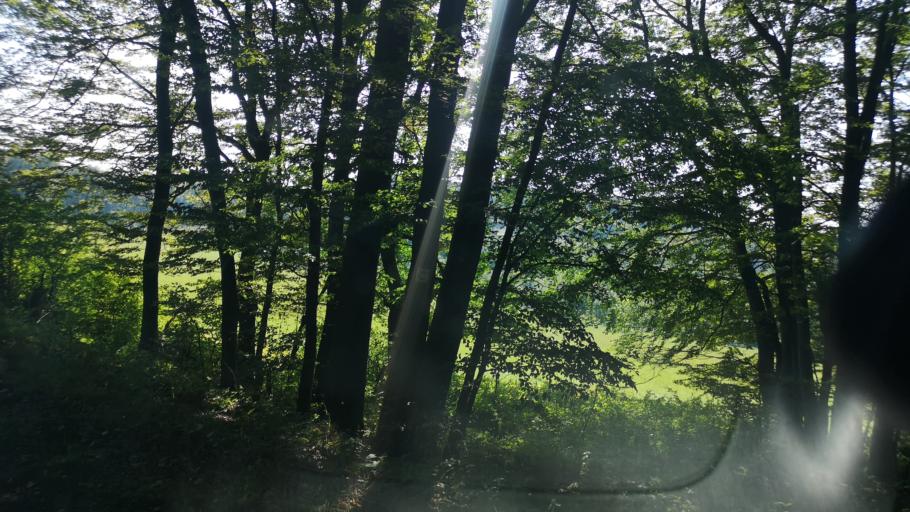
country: SK
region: Trnavsky
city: Smolenice
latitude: 48.5738
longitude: 17.4383
